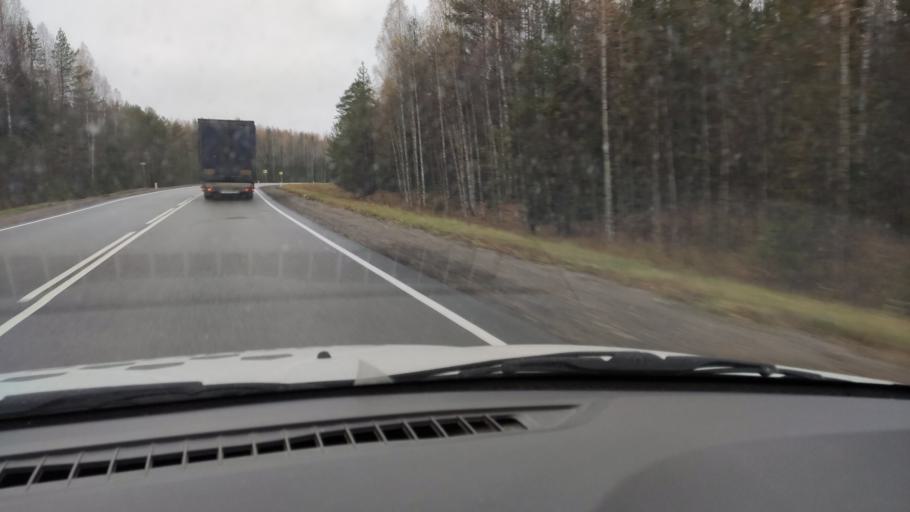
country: RU
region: Kirov
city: Chernaya Kholunitsa
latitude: 58.8296
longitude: 51.7650
